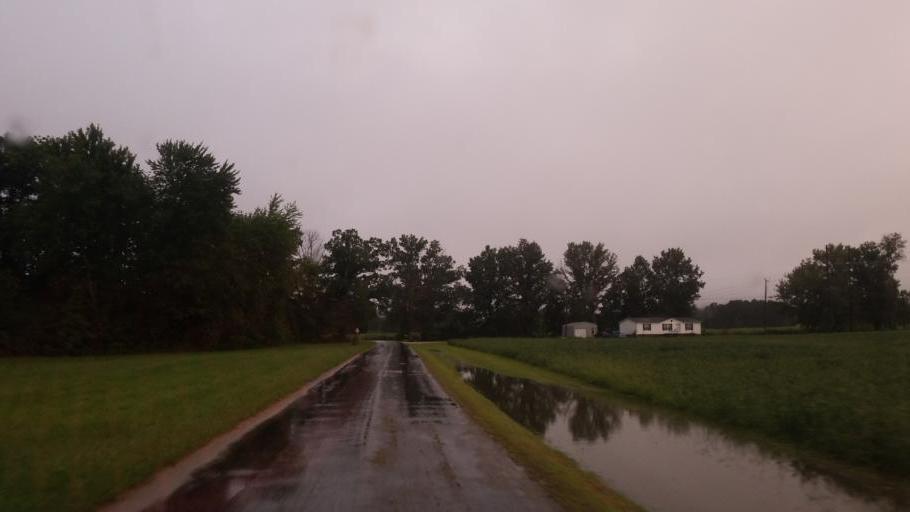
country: US
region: Kentucky
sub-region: Fleming County
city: Flemingsburg
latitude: 38.4495
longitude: -83.6264
